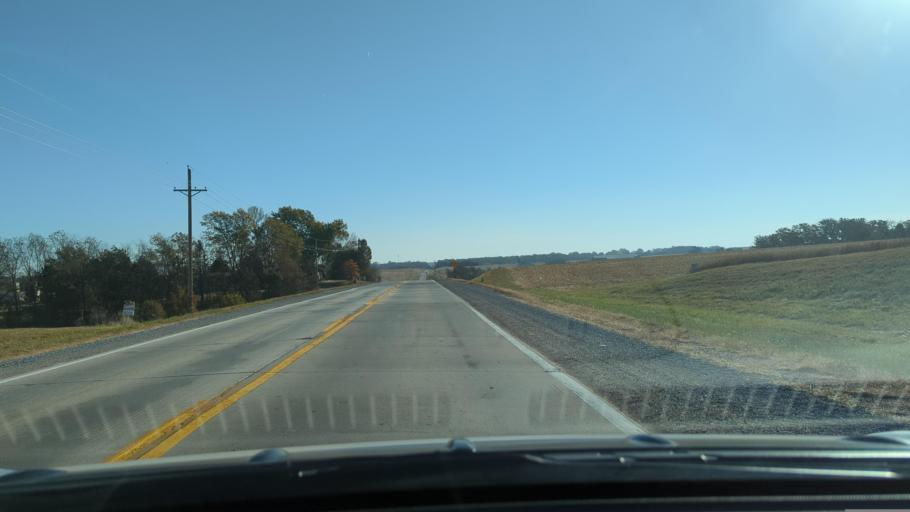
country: US
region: Nebraska
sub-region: Sarpy County
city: Papillion
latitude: 41.0927
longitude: -96.0146
